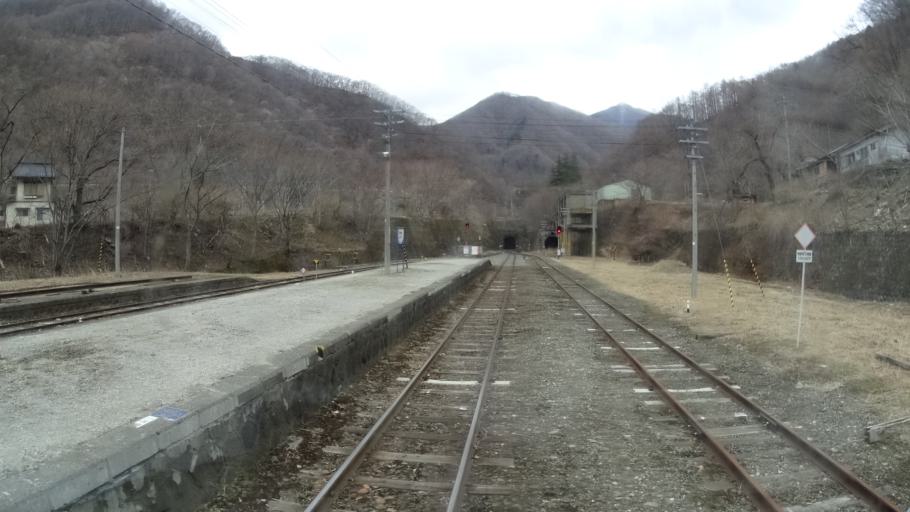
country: JP
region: Iwate
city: Kamaishi
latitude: 39.2807
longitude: 141.7183
